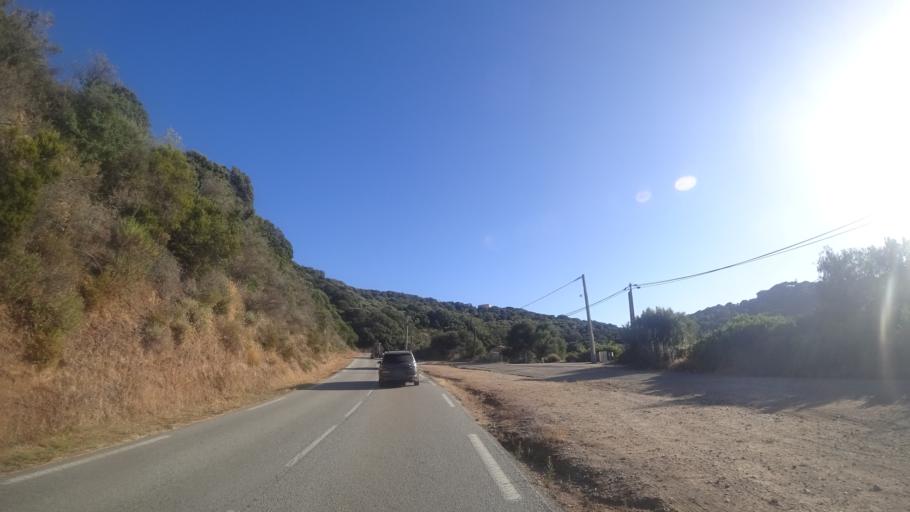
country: FR
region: Corsica
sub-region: Departement de la Corse-du-Sud
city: Cargese
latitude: 42.1650
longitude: 8.6021
